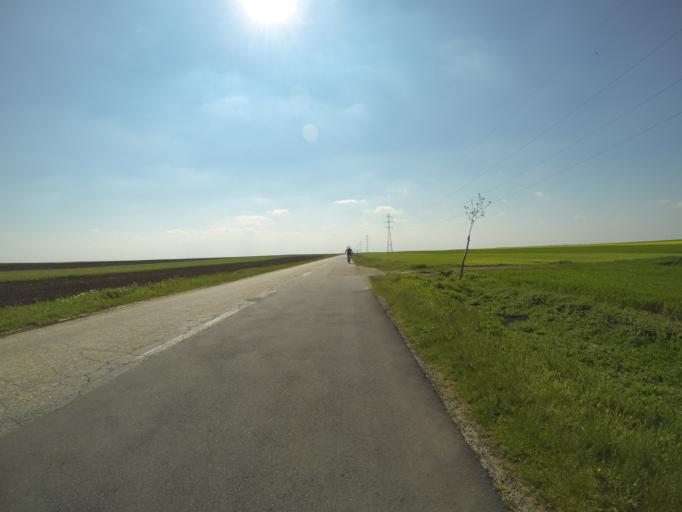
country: RO
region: Dolj
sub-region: Comuna Unirea
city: Unirea
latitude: 44.1604
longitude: 23.1446
